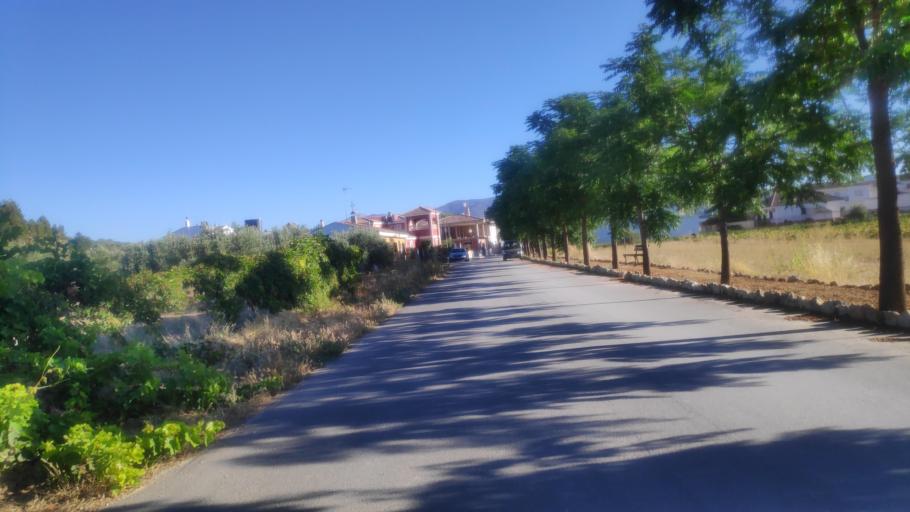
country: ES
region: Andalusia
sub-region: Provincia de Jaen
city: Pozo Alcon
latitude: 37.6700
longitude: -2.9716
